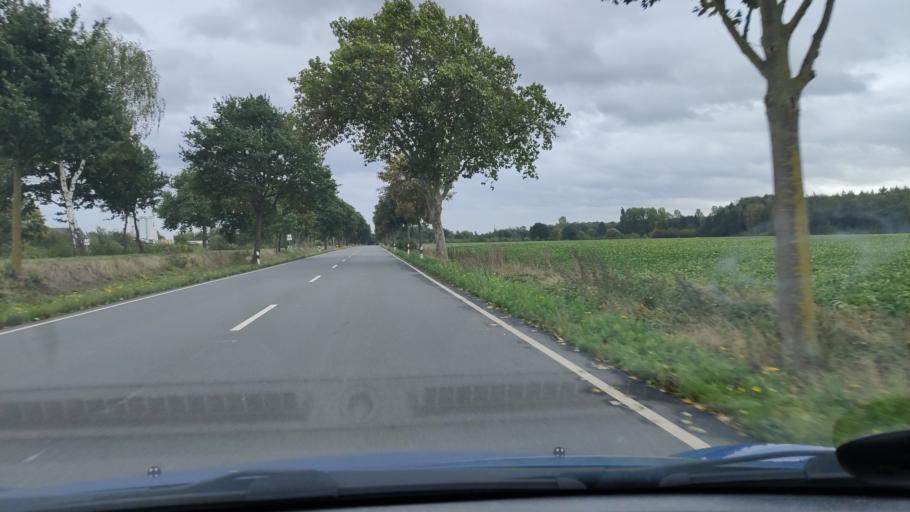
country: DE
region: Lower Saxony
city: Garbsen
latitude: 52.3945
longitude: 9.5651
